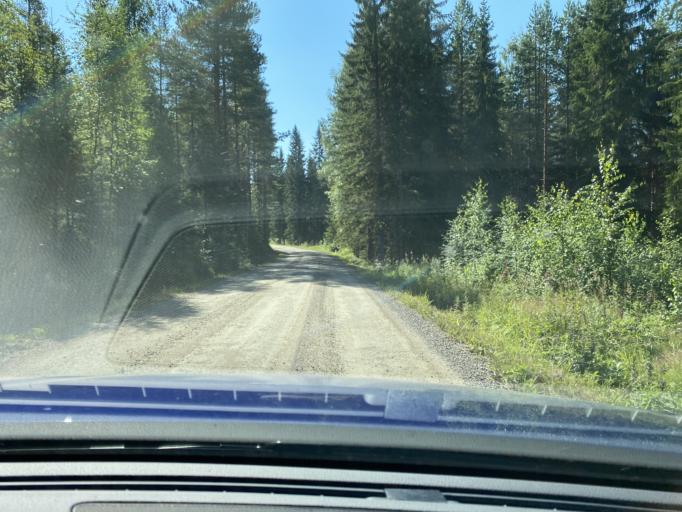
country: FI
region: Central Finland
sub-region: Jyvaeskylae
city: Korpilahti
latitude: 61.8784
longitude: 25.4112
